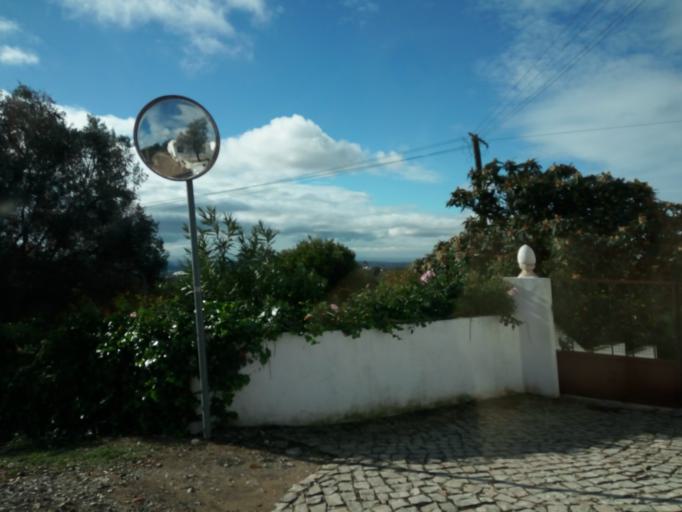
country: PT
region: Faro
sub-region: Faro
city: Santa Barbara de Nexe
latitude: 37.1100
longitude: -7.9635
